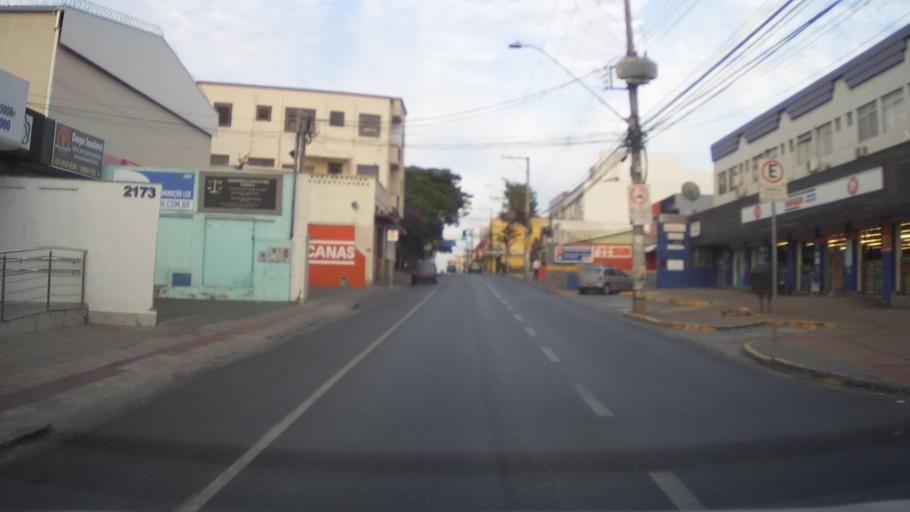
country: BR
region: Minas Gerais
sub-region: Belo Horizonte
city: Belo Horizonte
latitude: -19.9151
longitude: -43.9732
